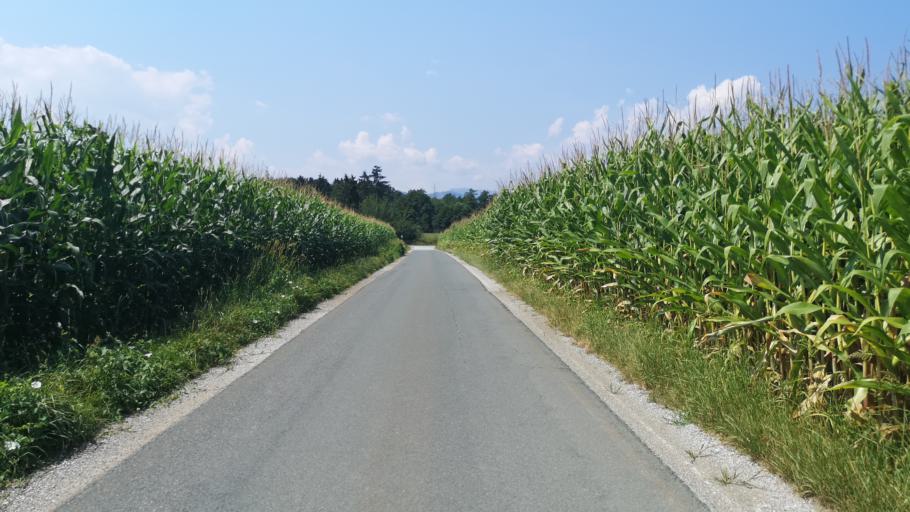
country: AT
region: Styria
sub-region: Politischer Bezirk Deutschlandsberg
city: Gross Sankt Florian
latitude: 46.8165
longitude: 15.2897
